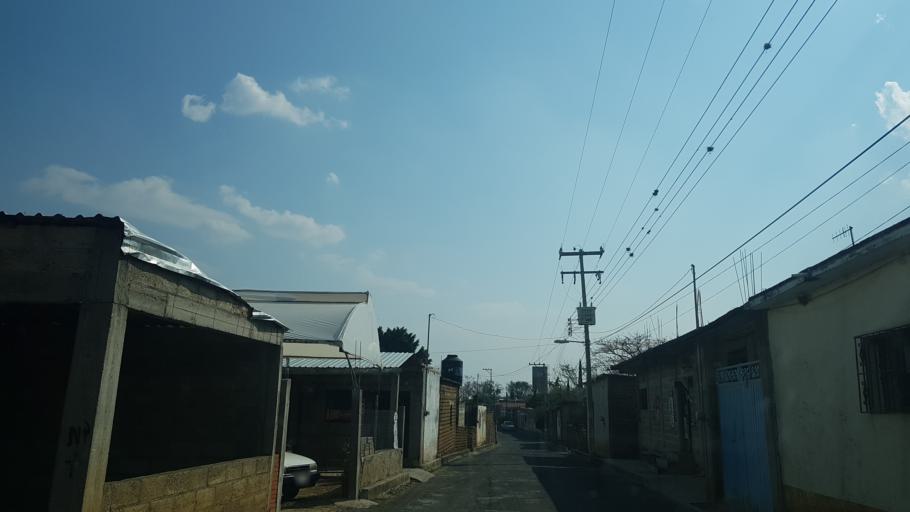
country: MX
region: Morelos
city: Tlacotepec
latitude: 18.8106
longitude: -98.7119
